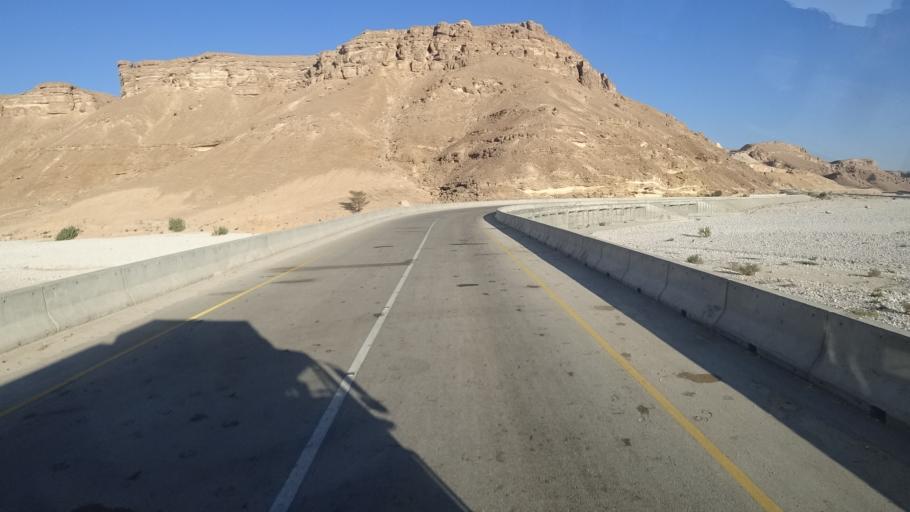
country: YE
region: Al Mahrah
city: Hawf
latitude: 17.0985
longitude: 53.0504
